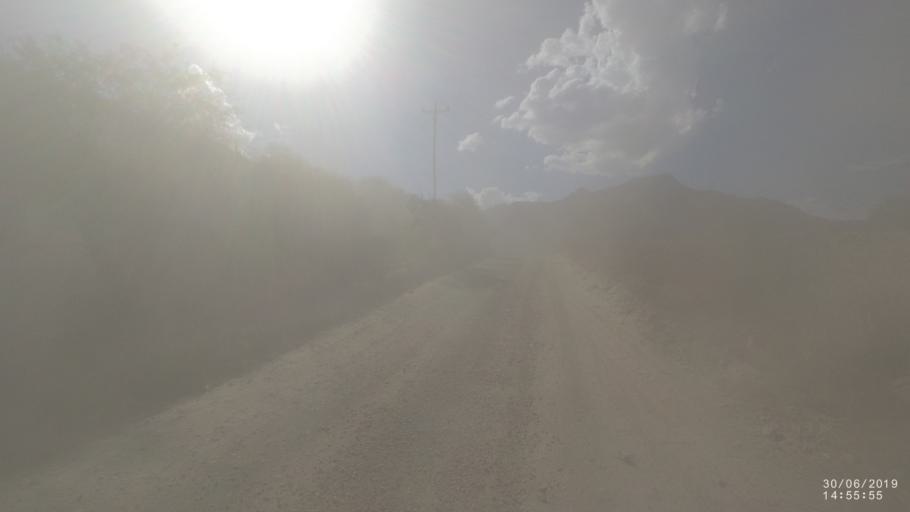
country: BO
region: Cochabamba
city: Irpa Irpa
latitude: -17.7517
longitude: -66.3525
